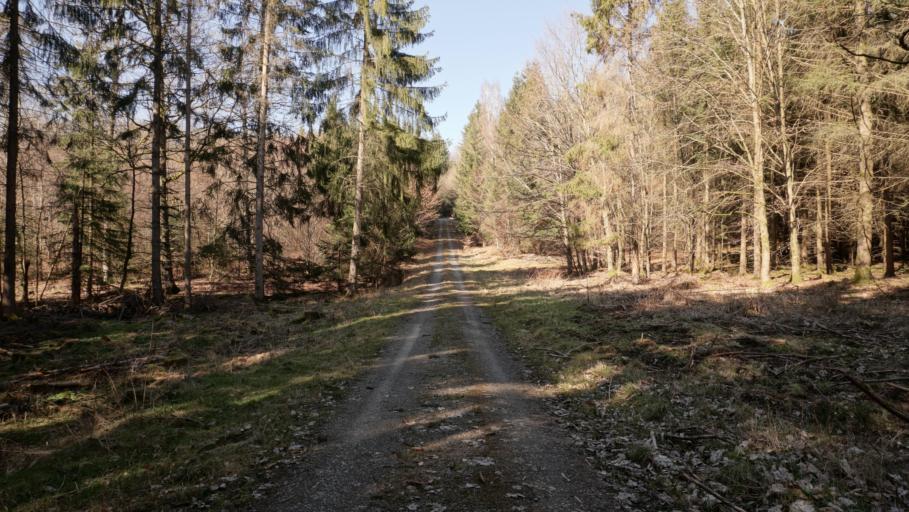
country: DE
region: Baden-Wuerttemberg
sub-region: Karlsruhe Region
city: Fahrenbach
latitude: 49.4443
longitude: 9.1371
